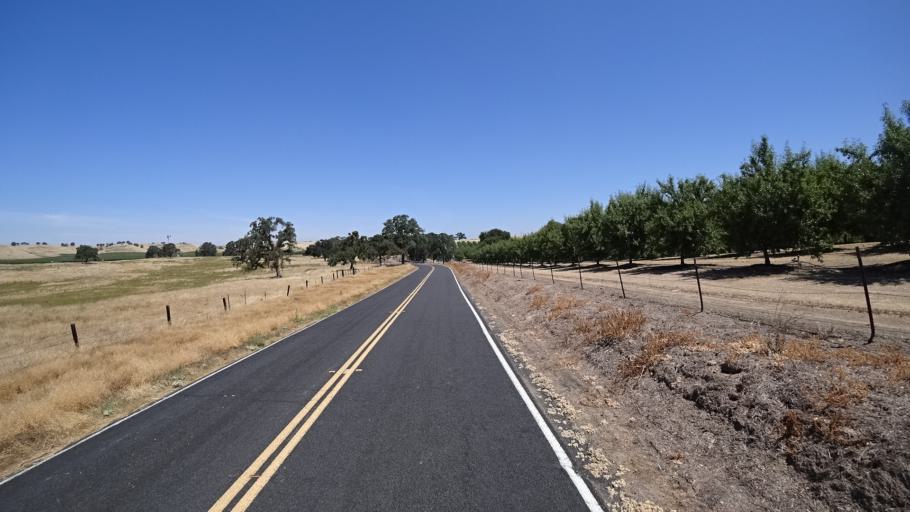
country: US
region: California
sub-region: Calaveras County
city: Rancho Calaveras
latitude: 38.1009
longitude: -120.9449
